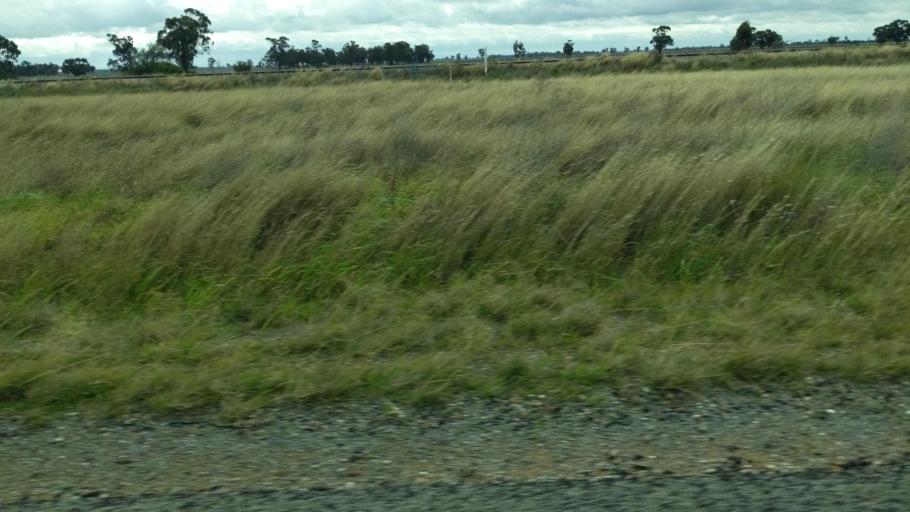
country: AU
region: New South Wales
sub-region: Coolamon
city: Coolamon
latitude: -34.7593
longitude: 146.8786
